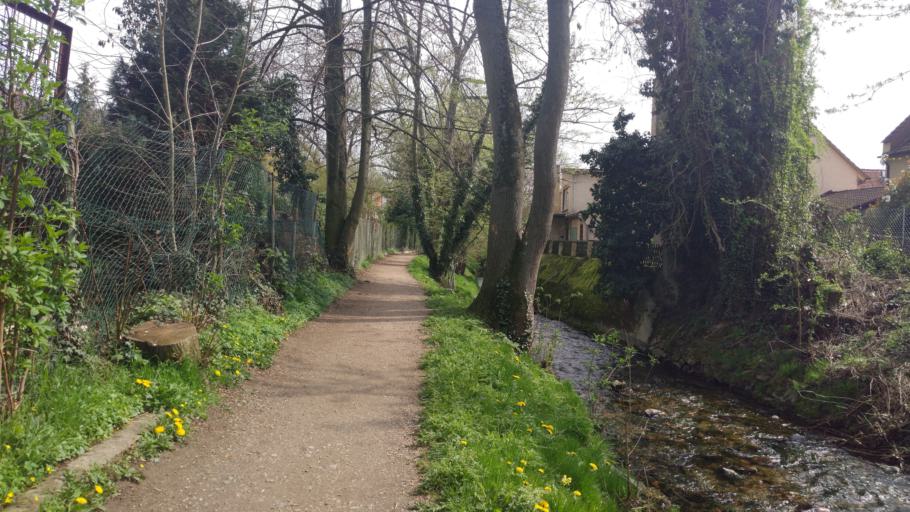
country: DE
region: Hesse
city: Sulzbach
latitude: 50.1115
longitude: 8.5319
